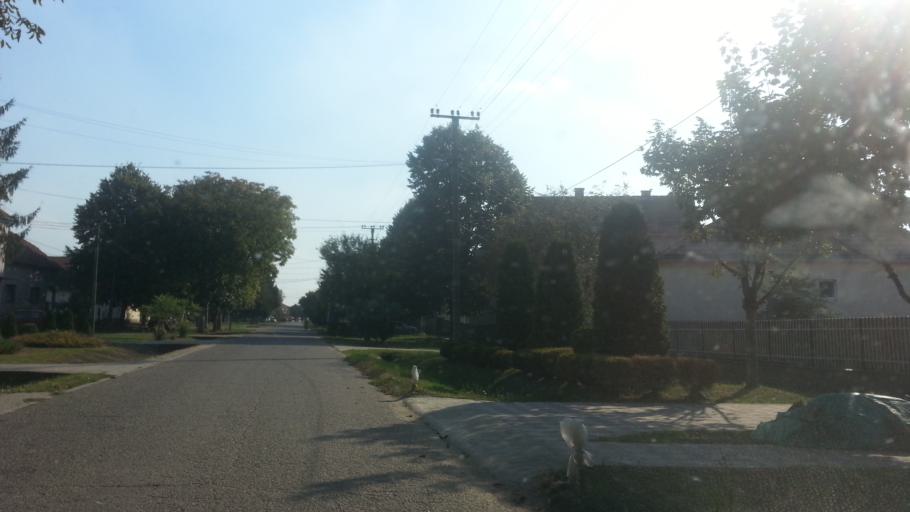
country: RS
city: Stari Banovci
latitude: 44.9882
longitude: 20.2742
